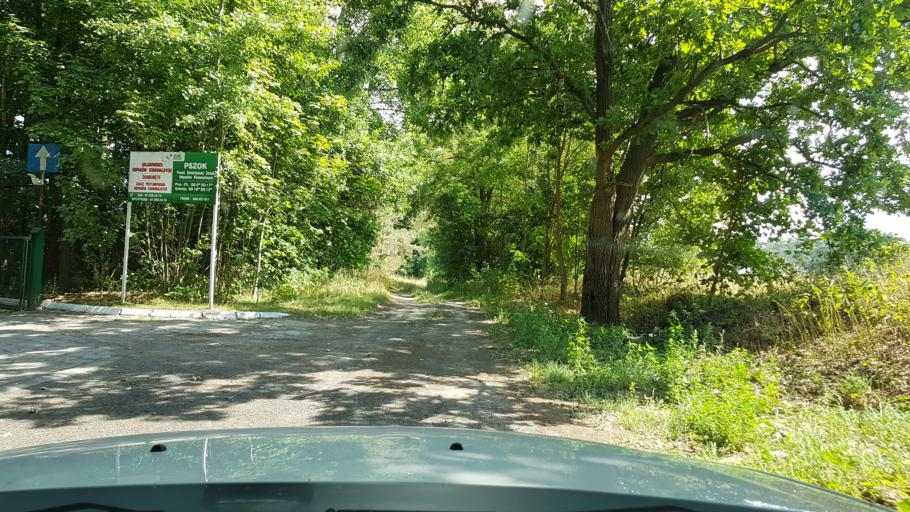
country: PL
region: West Pomeranian Voivodeship
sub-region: Powiat walecki
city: Walcz
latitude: 53.2543
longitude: 16.5079
